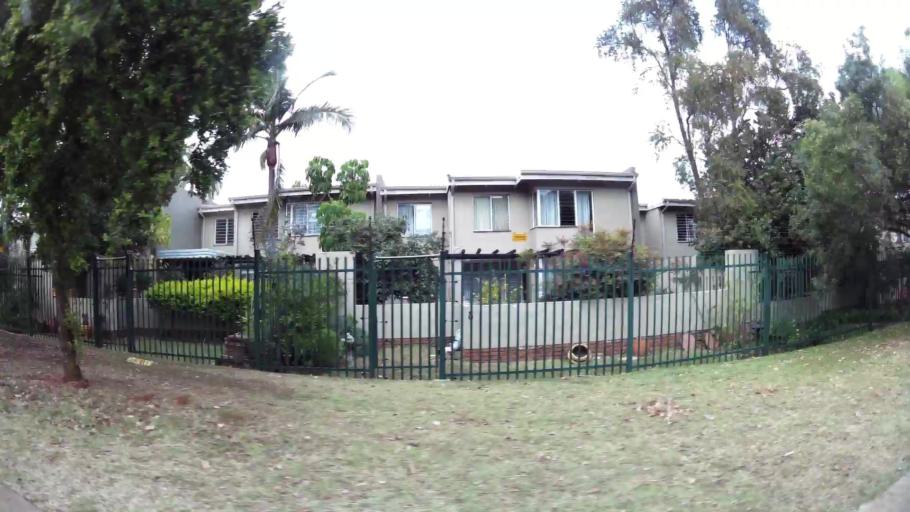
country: ZA
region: Gauteng
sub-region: City of Tshwane Metropolitan Municipality
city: Pretoria
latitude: -25.7494
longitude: 28.3133
